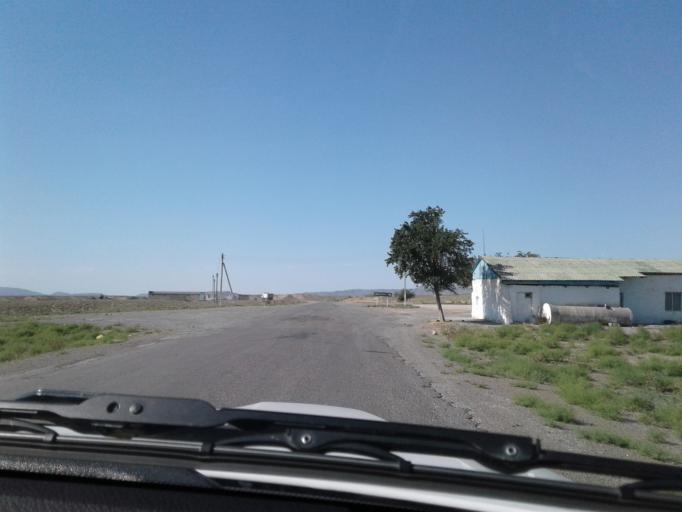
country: TM
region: Balkan
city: Serdar
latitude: 38.7209
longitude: 56.2932
